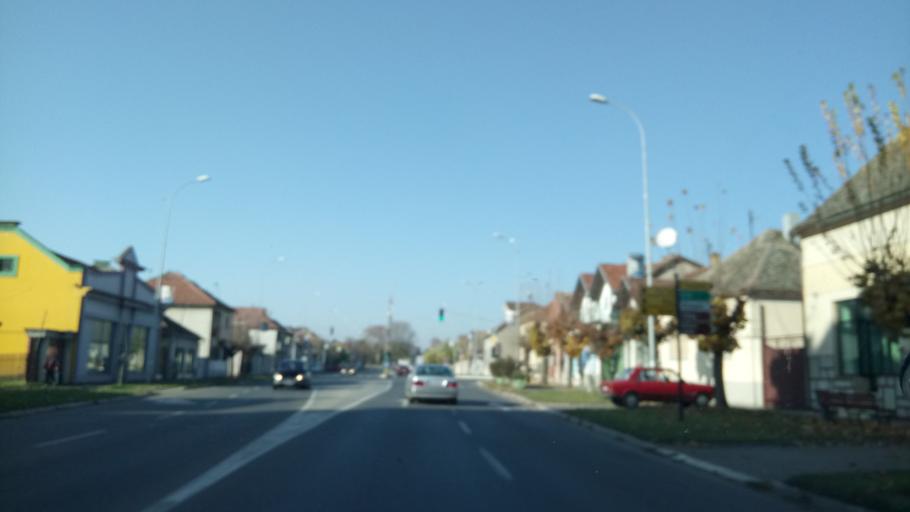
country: RS
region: Autonomna Pokrajina Vojvodina
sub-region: Sremski Okrug
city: Ingija
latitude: 45.0504
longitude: 20.0779
